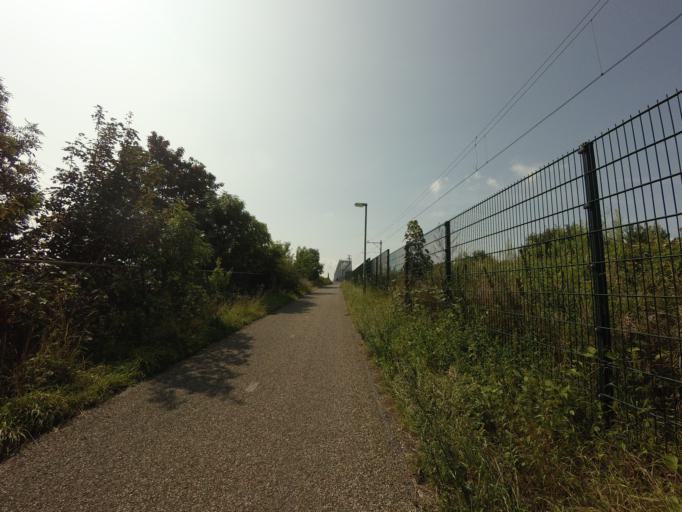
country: NL
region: South Holland
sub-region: Gemeente Sliedrecht
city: Sliedrecht
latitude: 51.8246
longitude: 4.7418
